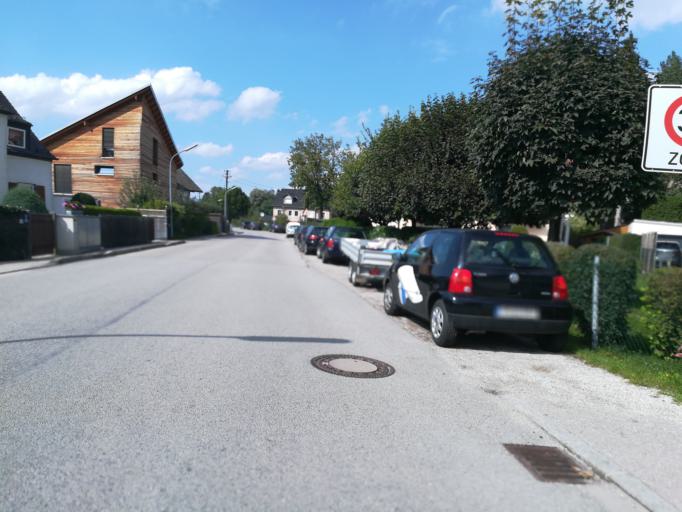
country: DE
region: Bavaria
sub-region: Upper Bavaria
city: Oberschleissheim
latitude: 48.2183
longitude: 11.5246
